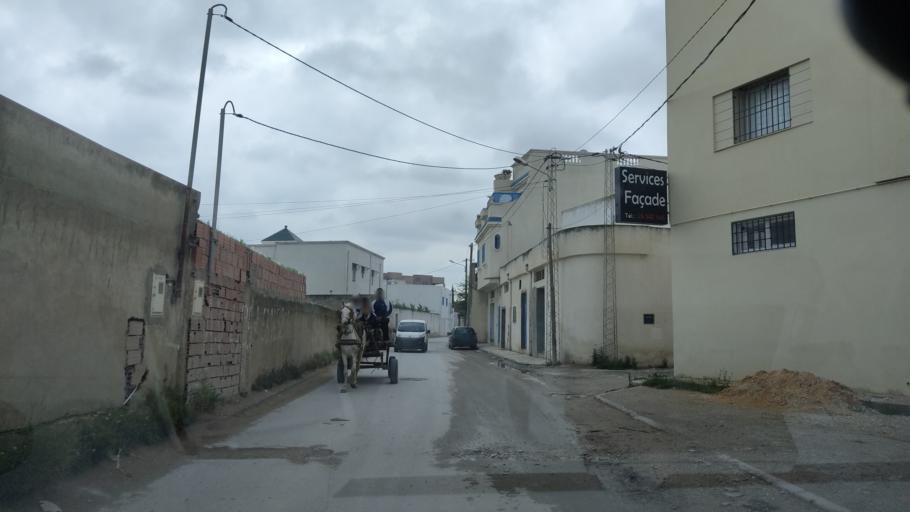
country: TN
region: Ariana
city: Ariana
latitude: 36.8831
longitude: 10.2188
